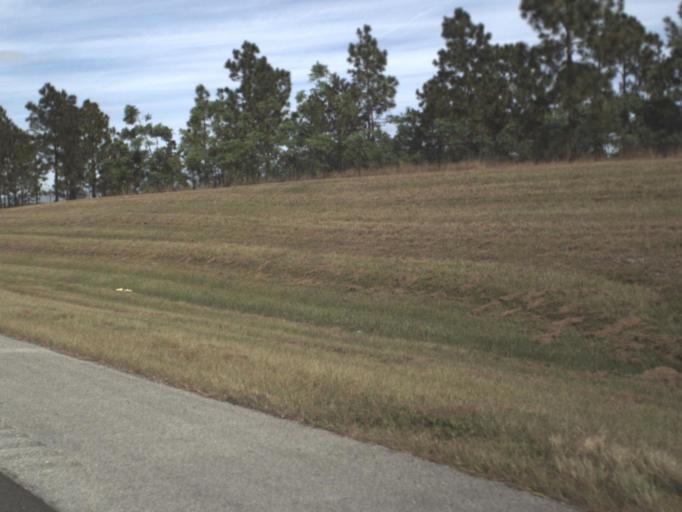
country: US
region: Florida
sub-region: Polk County
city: Citrus Ridge
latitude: 28.3975
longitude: -81.6210
